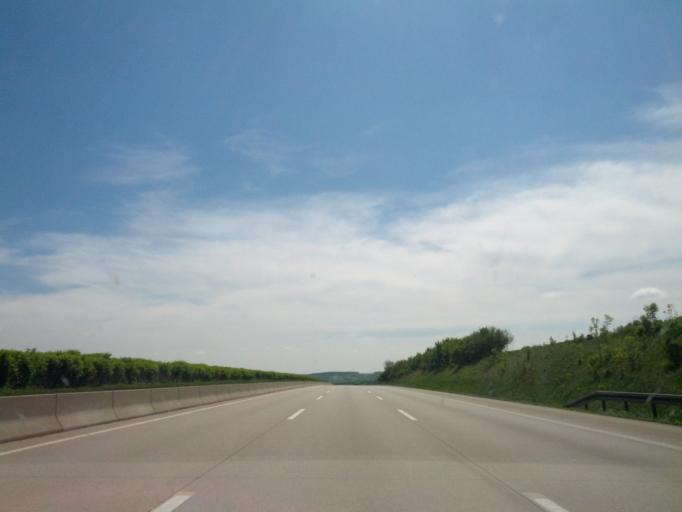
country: DE
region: Thuringia
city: Mellingen
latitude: 50.9154
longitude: 11.4113
